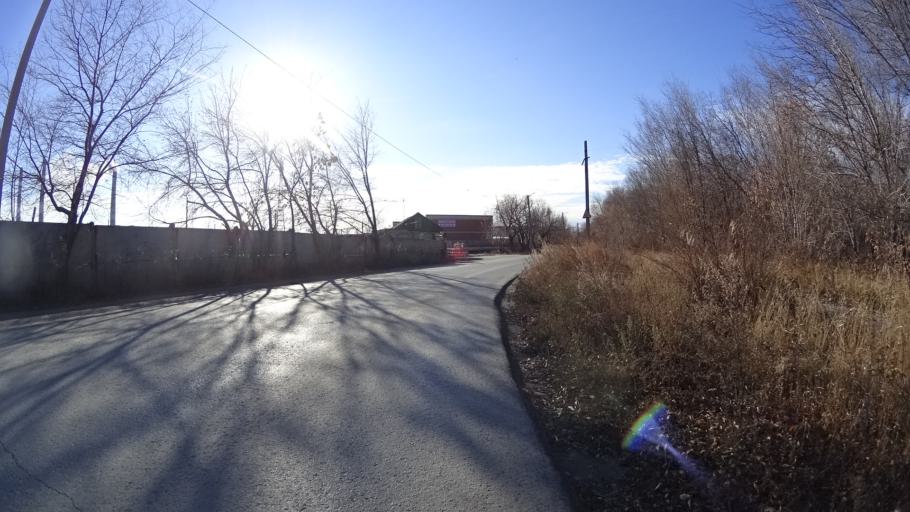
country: RU
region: Chelyabinsk
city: Troitsk
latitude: 54.0440
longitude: 61.6403
